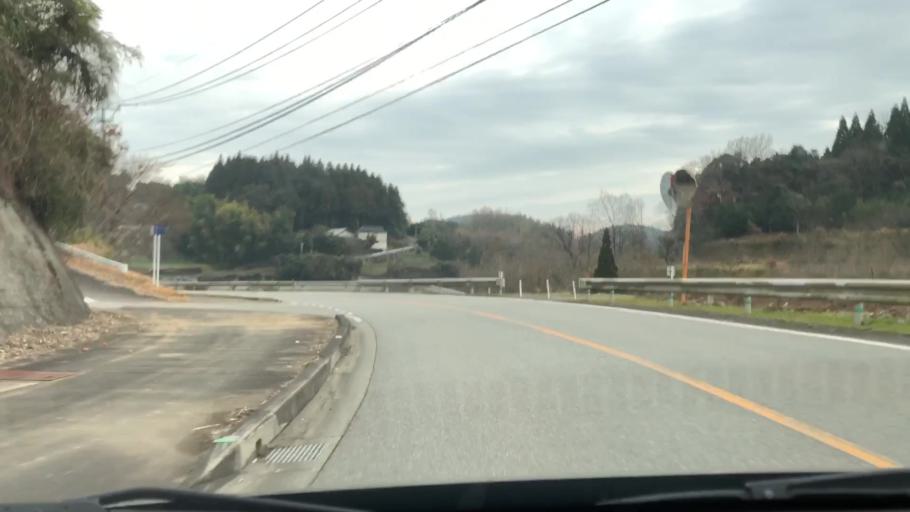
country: JP
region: Oita
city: Usuki
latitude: 33.0098
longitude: 131.6374
